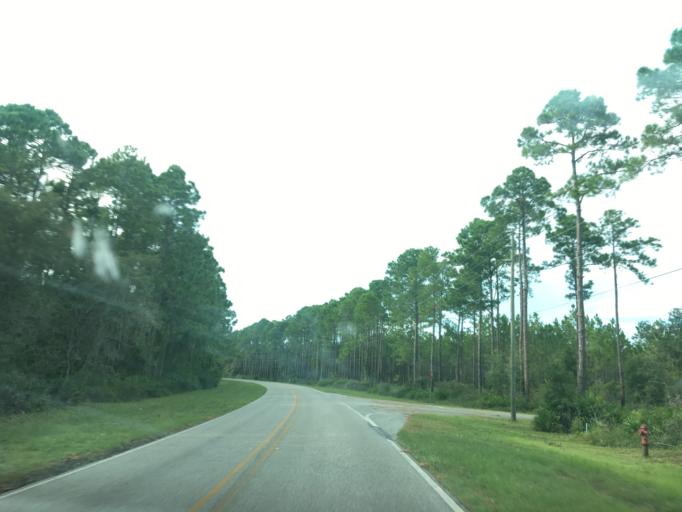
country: US
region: Florida
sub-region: Wakulla County
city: Crawfordville
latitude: 29.9347
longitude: -84.3785
